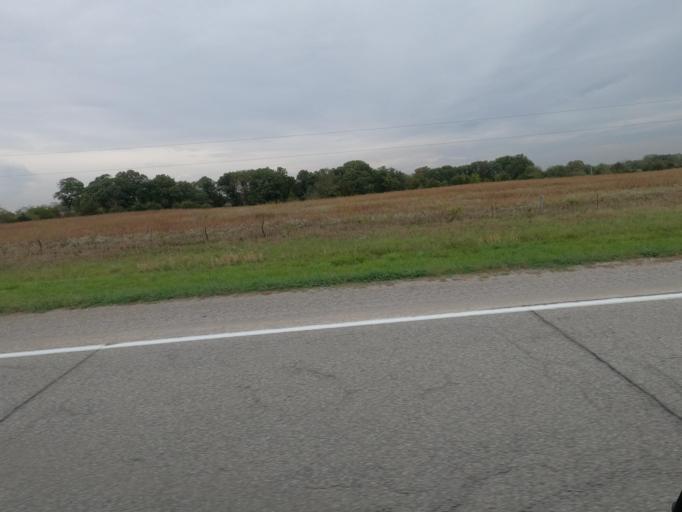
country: US
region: Iowa
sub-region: Van Buren County
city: Keosauqua
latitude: 40.8546
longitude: -92.0575
